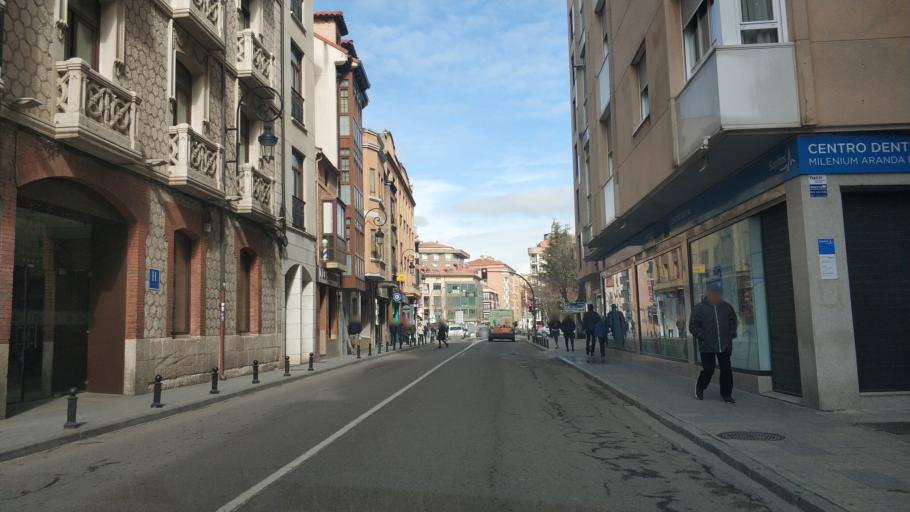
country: ES
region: Castille and Leon
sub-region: Provincia de Burgos
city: Aranda de Duero
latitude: 41.6722
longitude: -3.6853
